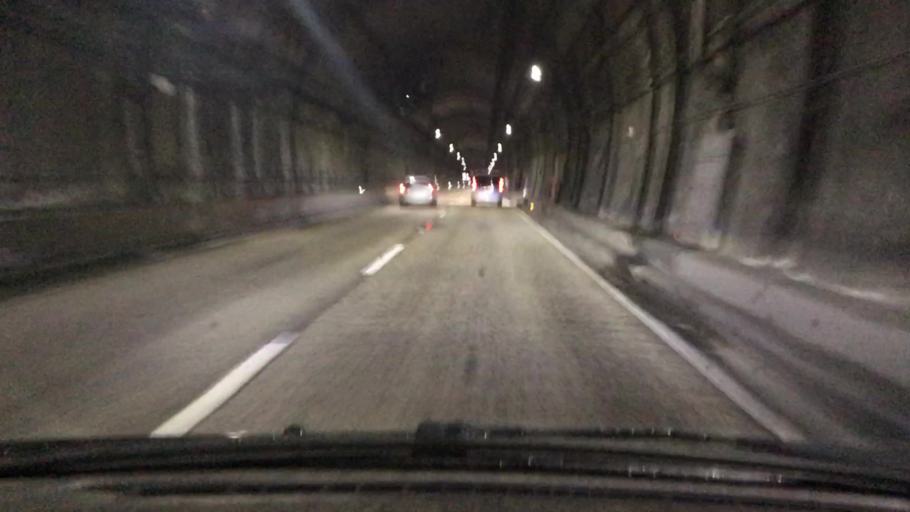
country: JP
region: Hyogo
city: Kobe
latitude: 34.7475
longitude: 135.1680
